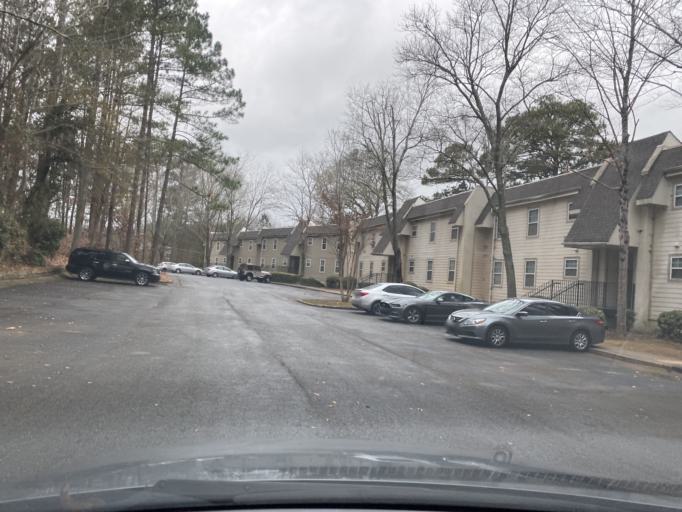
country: US
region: Georgia
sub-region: DeKalb County
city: Pine Mountain
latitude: 33.6951
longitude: -84.1444
